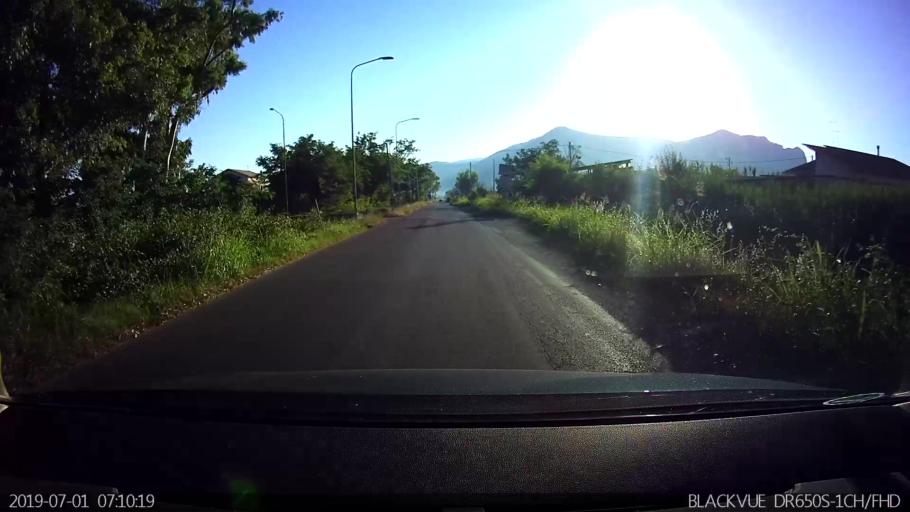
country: IT
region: Latium
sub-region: Provincia di Latina
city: Borgo Hermada
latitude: 41.3113
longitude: 13.1693
